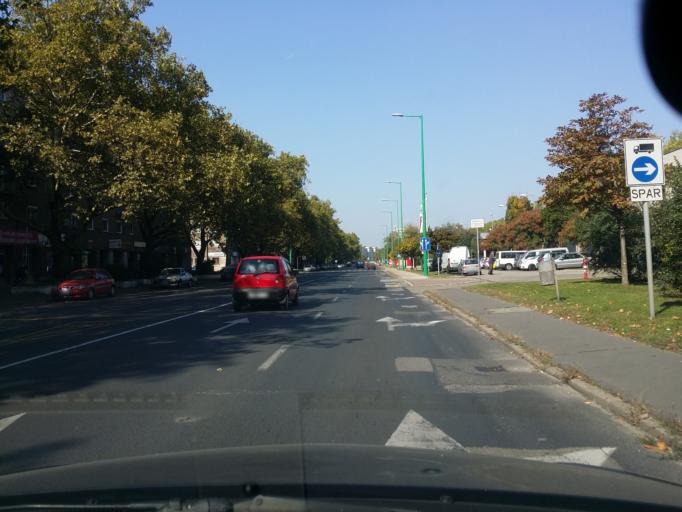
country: HU
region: Fejer
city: Dunaujvaros
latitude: 46.9601
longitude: 18.9440
